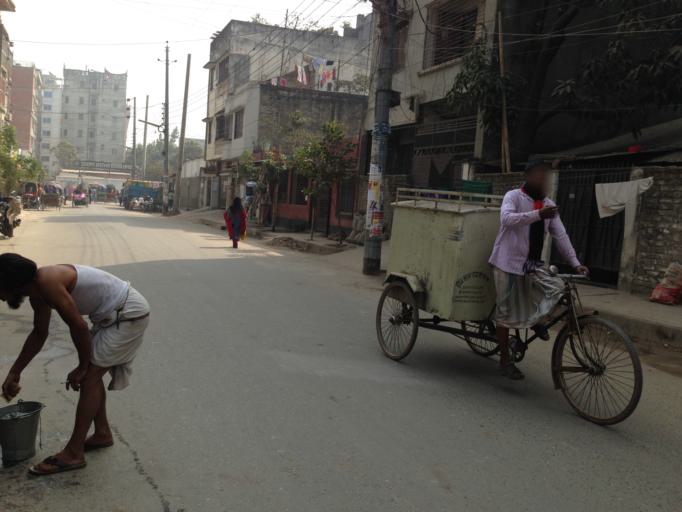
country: BD
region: Dhaka
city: Azimpur
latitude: 23.8055
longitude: 90.3791
